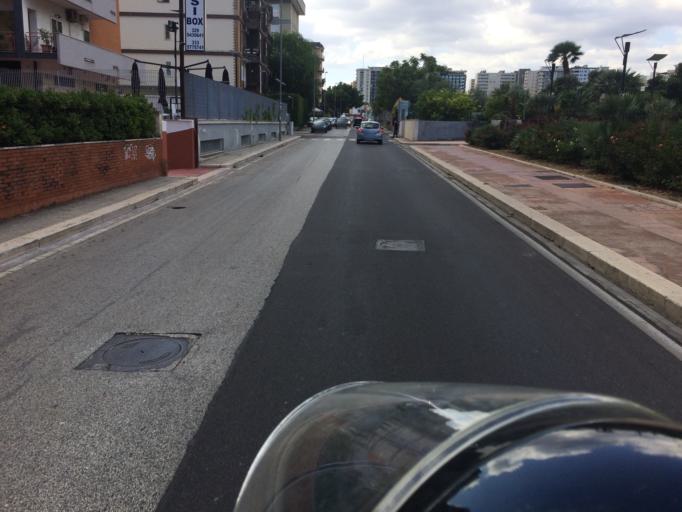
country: IT
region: Apulia
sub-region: Provincia di Bari
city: Bari
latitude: 41.1042
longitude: 16.8578
